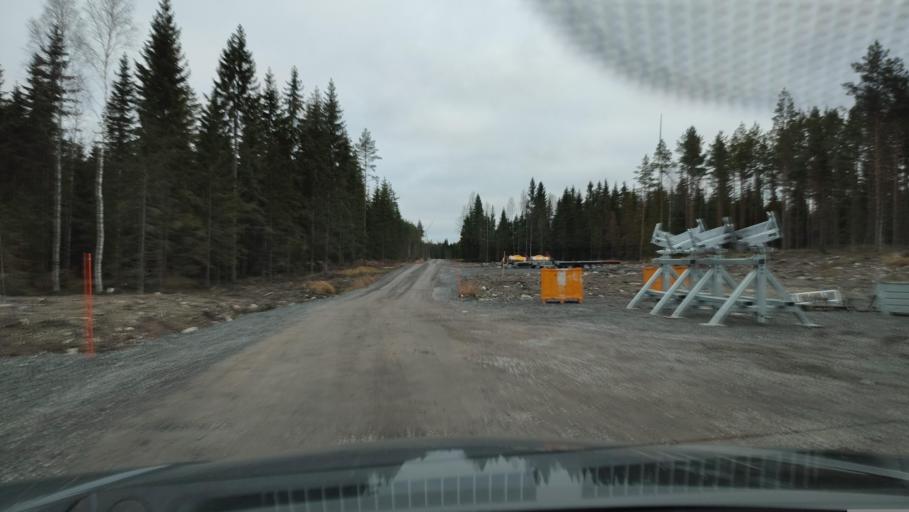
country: FI
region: Southern Ostrobothnia
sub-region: Suupohja
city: Karijoki
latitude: 62.1808
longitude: 21.5585
